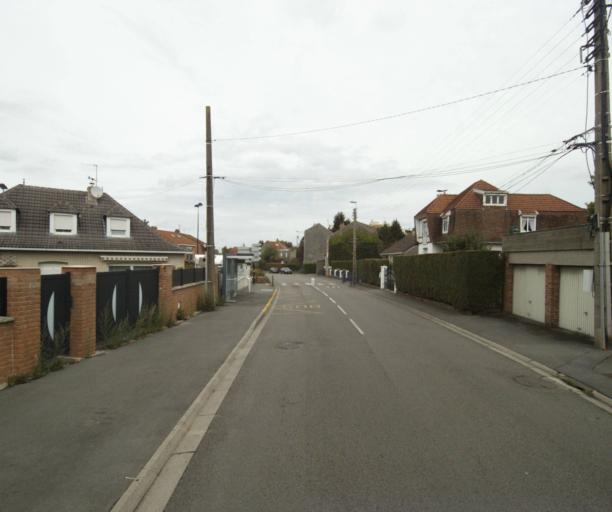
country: FR
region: Nord-Pas-de-Calais
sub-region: Departement du Nord
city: Ronchin
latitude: 50.5953
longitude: 3.0806
